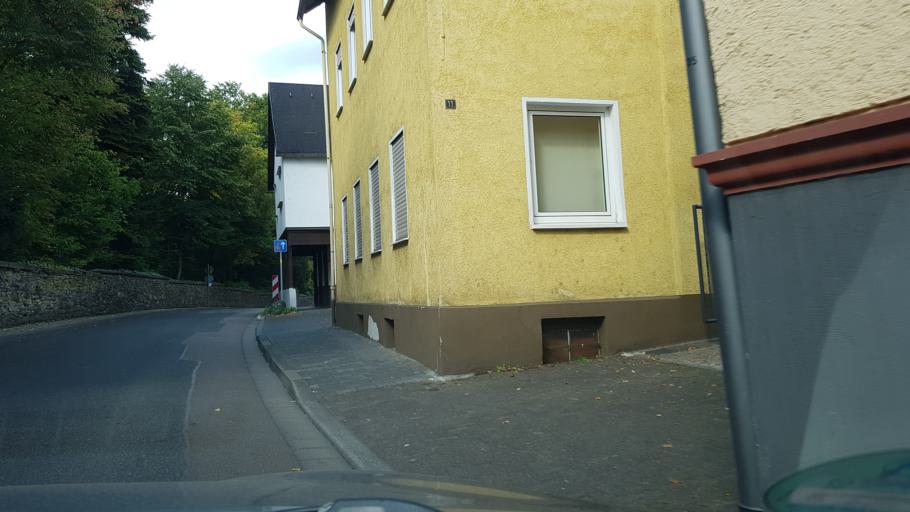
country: DE
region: Rheinland-Pfalz
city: Nassau
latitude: 50.3142
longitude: 7.7975
